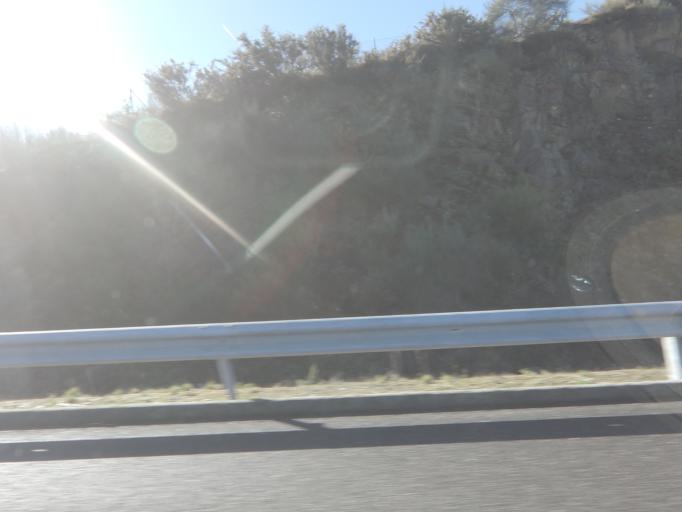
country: ES
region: Galicia
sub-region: Provincia de Pontevedra
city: Dozon
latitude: 42.5631
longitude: -8.0383
